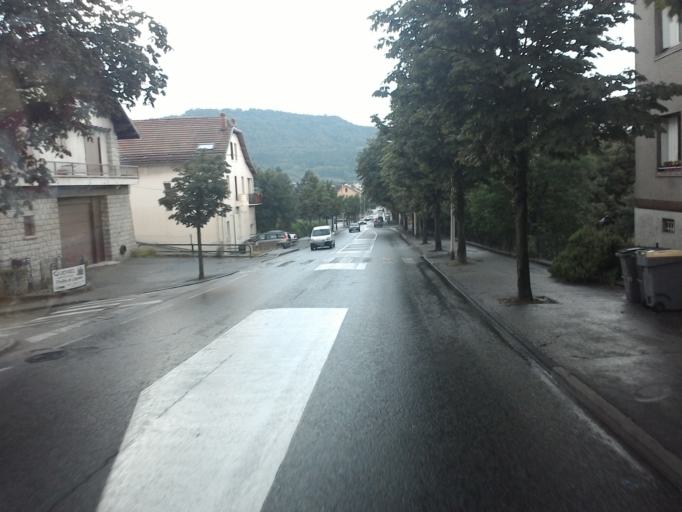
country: FR
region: Provence-Alpes-Cote d'Azur
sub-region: Departement des Hautes-Alpes
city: Gap
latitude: 44.5673
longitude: 6.0835
